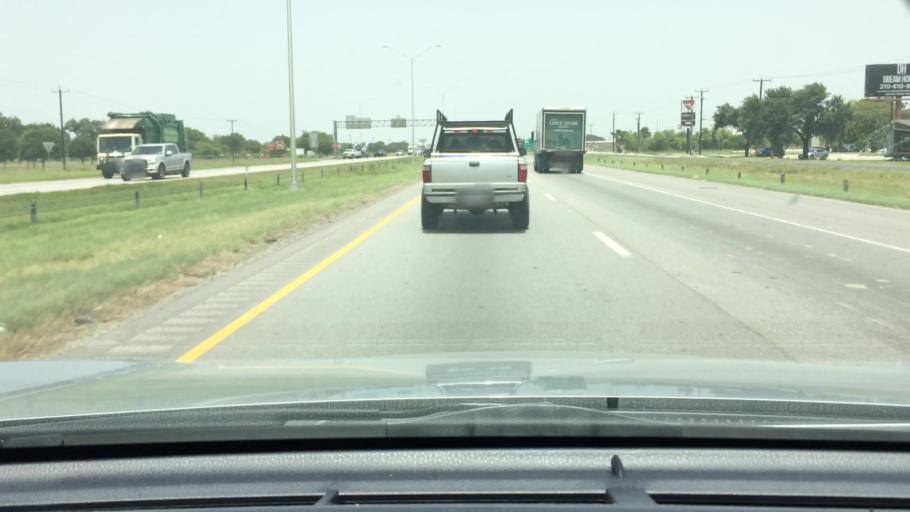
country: US
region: Texas
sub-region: Bexar County
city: China Grove
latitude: 29.4071
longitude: -98.3893
